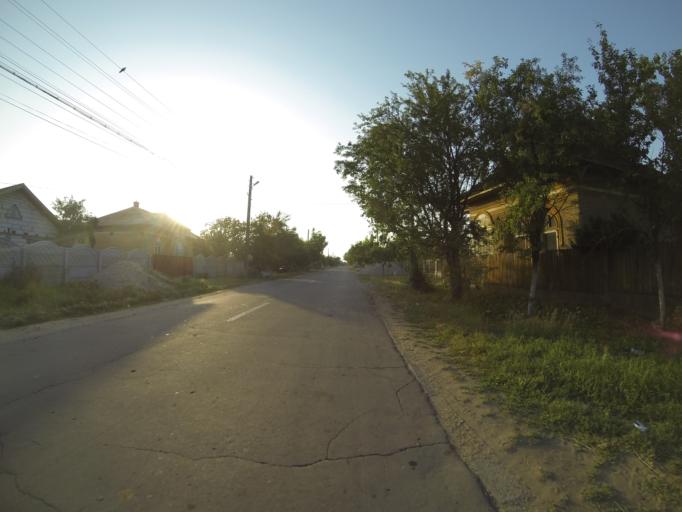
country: RO
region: Dolj
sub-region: Comuna Dobrotesti
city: Dobrotesti
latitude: 43.9618
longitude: 24.1135
